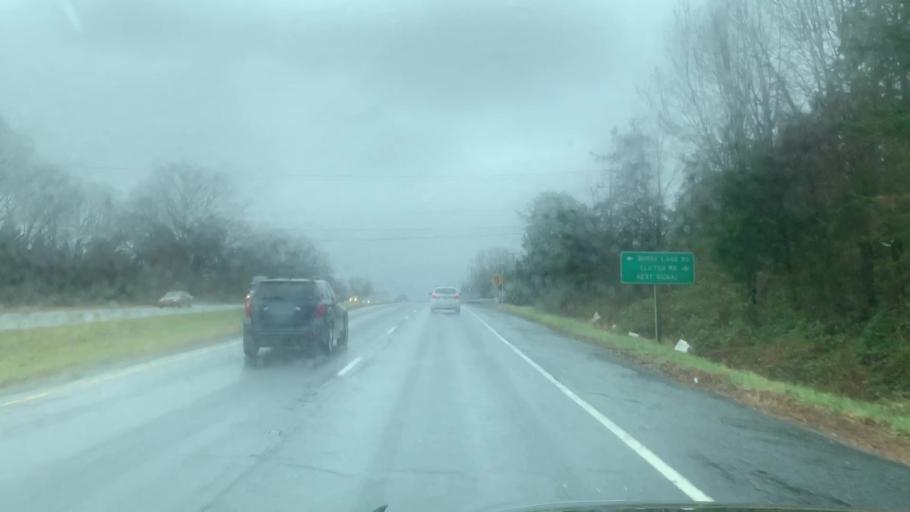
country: US
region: Virginia
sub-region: Fairfax County
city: Fairfax Station
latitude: 38.7693
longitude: -77.3168
